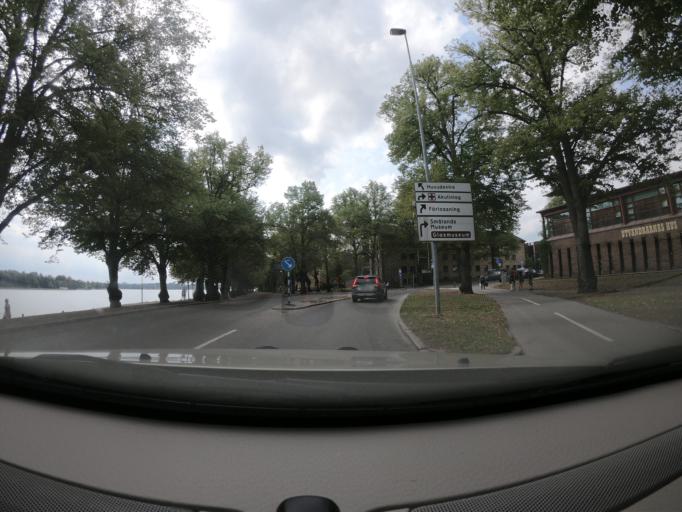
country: SE
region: Kronoberg
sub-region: Vaxjo Kommun
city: Vaexjoe
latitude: 56.8756
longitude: 14.8097
